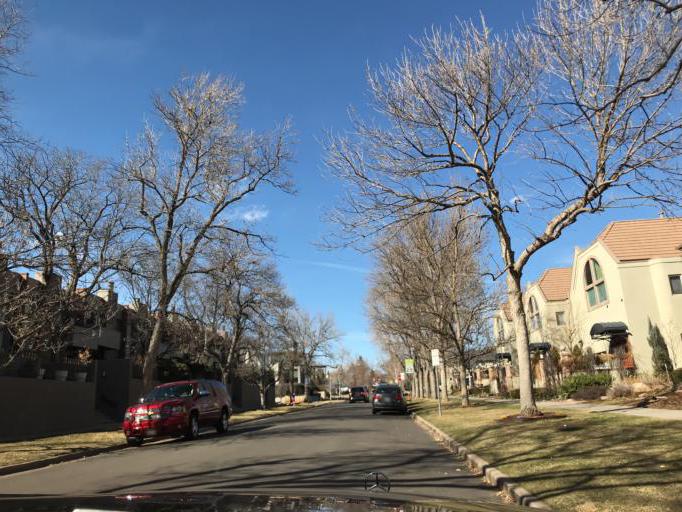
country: US
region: Colorado
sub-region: Arapahoe County
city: Glendale
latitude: 39.7233
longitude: -104.9570
